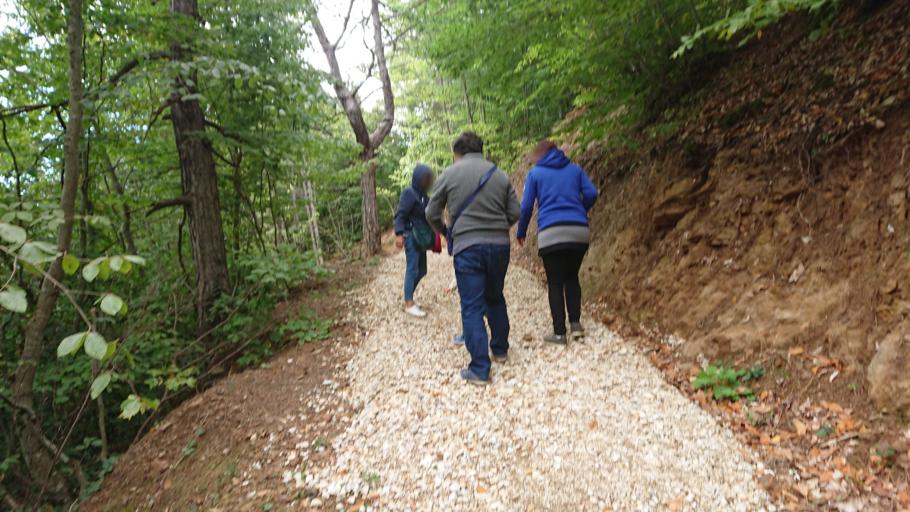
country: TR
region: Bilecik
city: Pazaryeri
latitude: 40.0131
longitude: 29.7941
